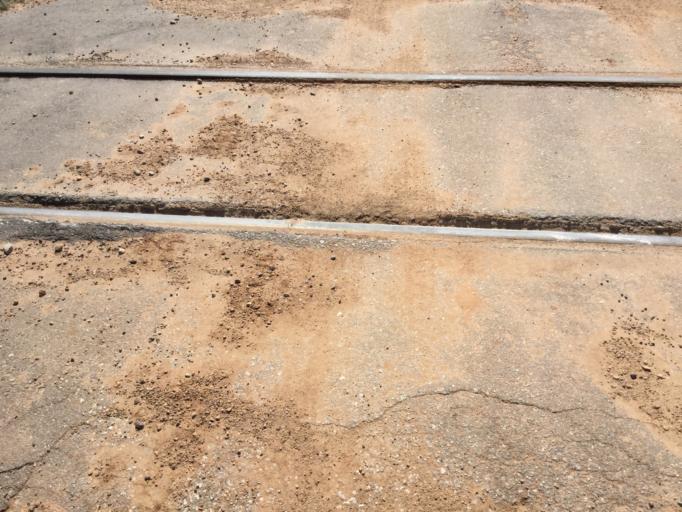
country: US
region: Kansas
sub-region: Barber County
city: Medicine Lodge
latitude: 37.2441
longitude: -98.3673
